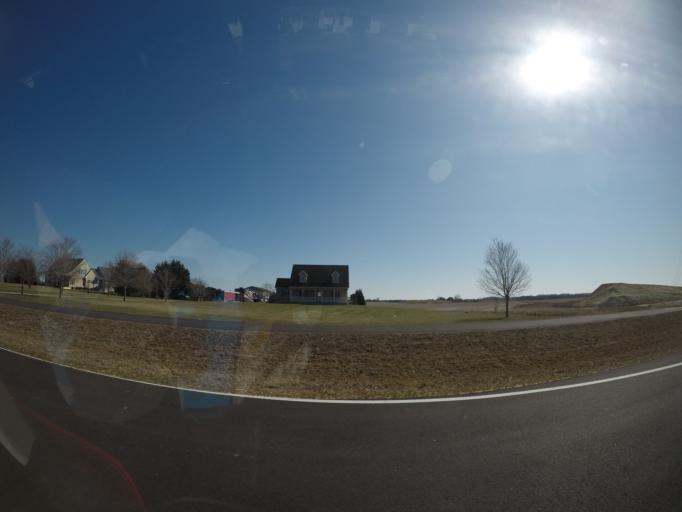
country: US
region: Delaware
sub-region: New Castle County
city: Middletown
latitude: 39.5083
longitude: -75.6813
